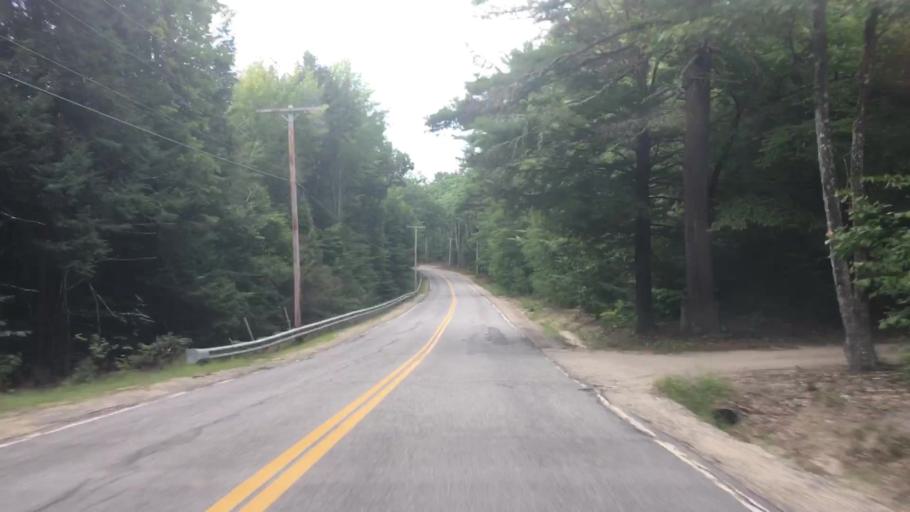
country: US
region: Maine
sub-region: Oxford County
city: Oxford
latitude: 44.0283
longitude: -70.5309
